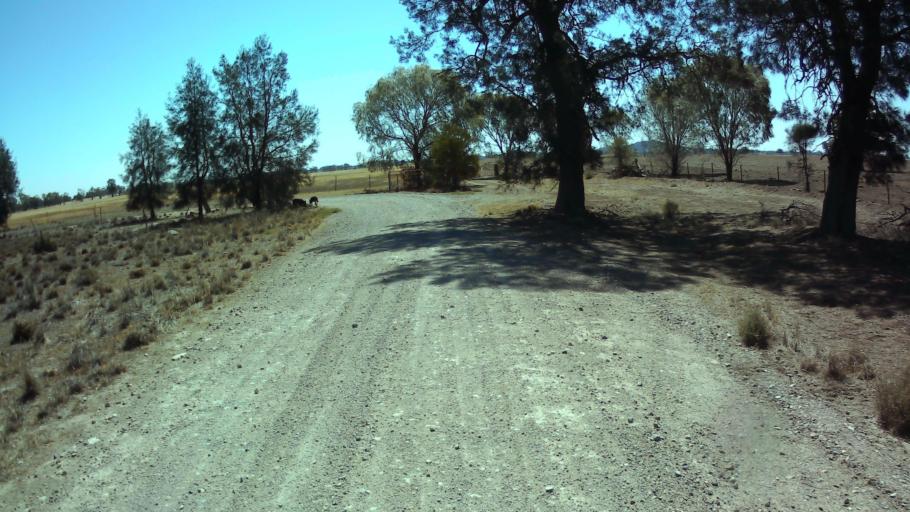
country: AU
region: New South Wales
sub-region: Forbes
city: Forbes
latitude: -33.7458
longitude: 147.7141
